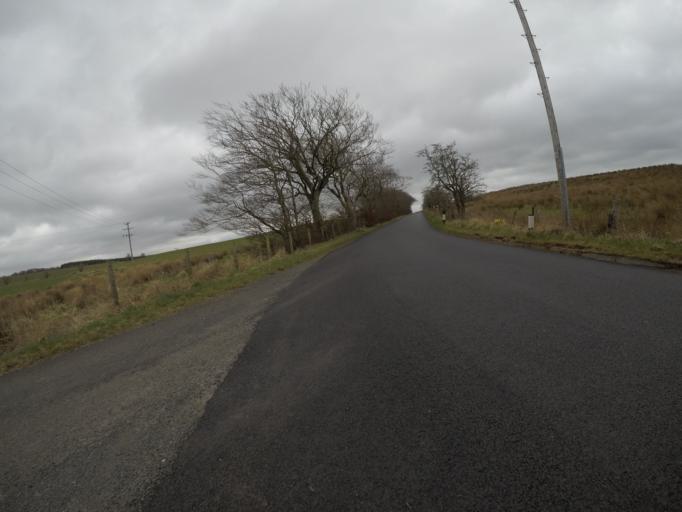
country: GB
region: Scotland
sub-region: East Ayrshire
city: Stewarton
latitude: 55.6822
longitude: -4.4608
